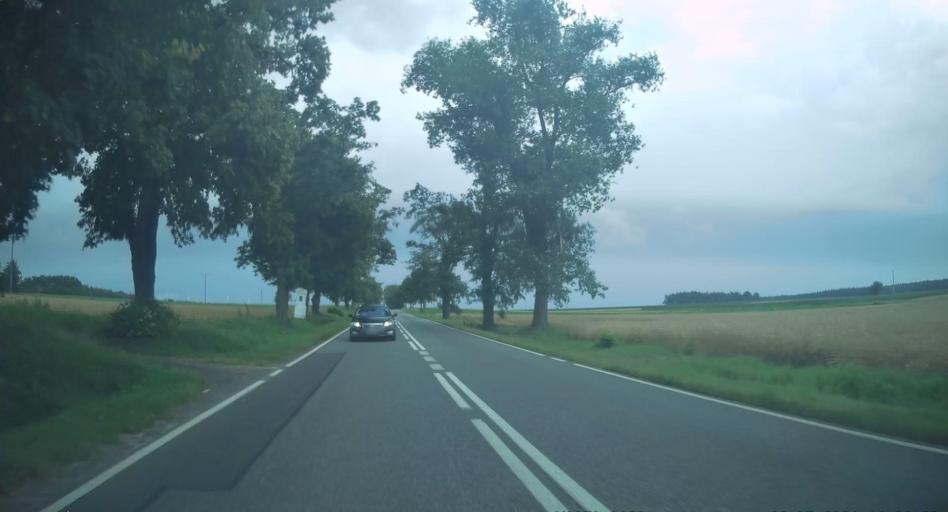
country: PL
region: Lodz Voivodeship
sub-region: Powiat skierniewicki
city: Gluchow
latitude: 51.7779
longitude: 20.1017
